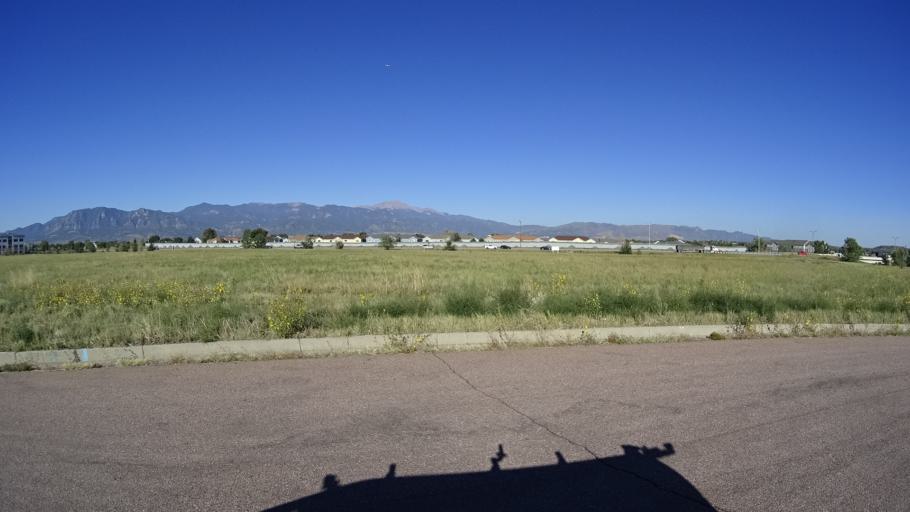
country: US
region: Colorado
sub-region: El Paso County
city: Cimarron Hills
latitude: 38.8203
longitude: -104.7250
